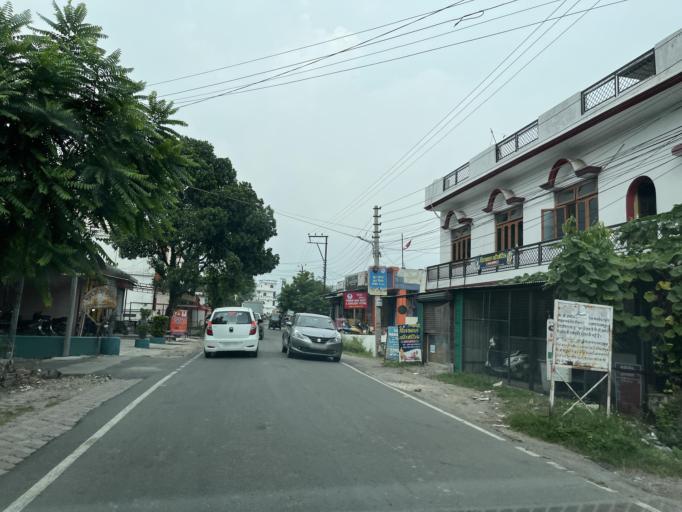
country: IN
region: Uttarakhand
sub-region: Naini Tal
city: Haldwani
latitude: 29.2065
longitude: 79.4933
